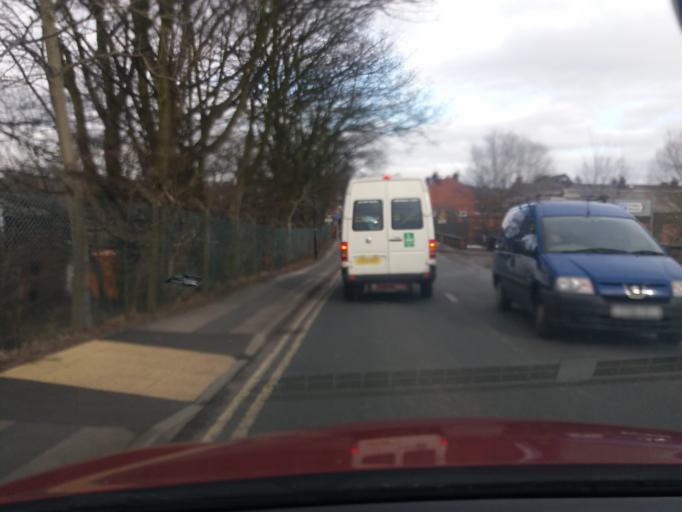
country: GB
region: England
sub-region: Lancashire
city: Chorley
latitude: 53.6562
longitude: -2.6265
